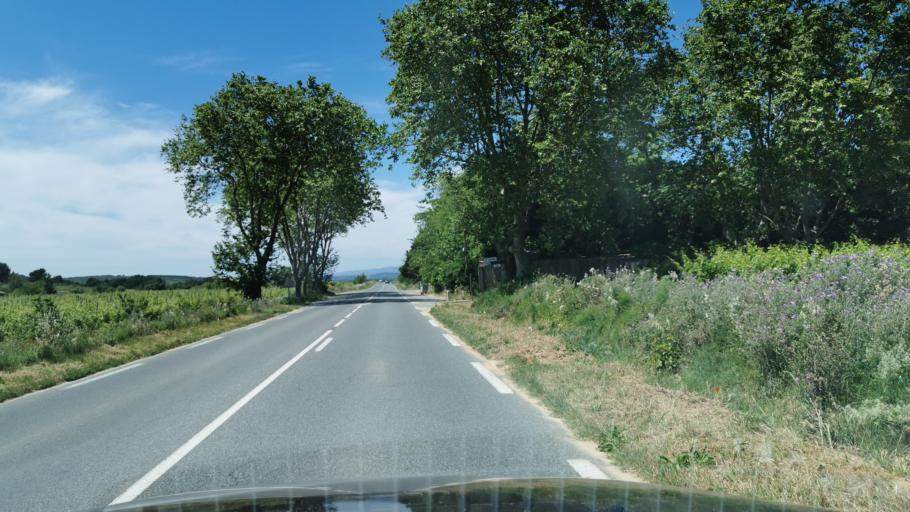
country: FR
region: Languedoc-Roussillon
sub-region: Departement de l'Aude
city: Moussan
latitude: 43.2068
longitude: 2.9561
